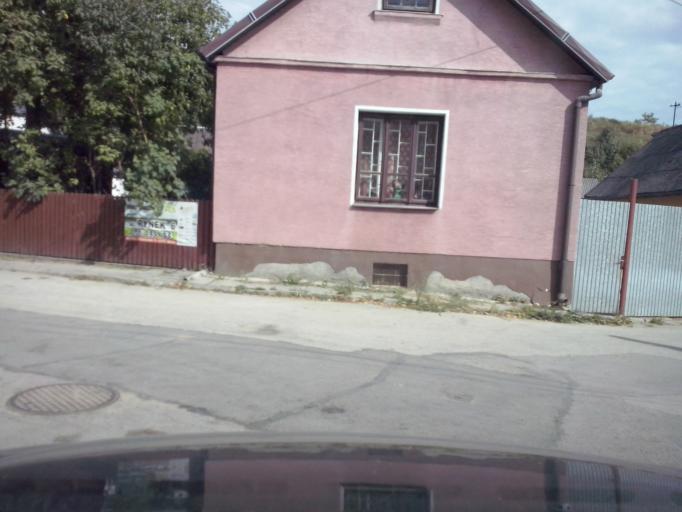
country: PL
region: Swietokrzyskie
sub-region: Powiat kielecki
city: Lagow
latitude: 50.7798
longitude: 21.0870
